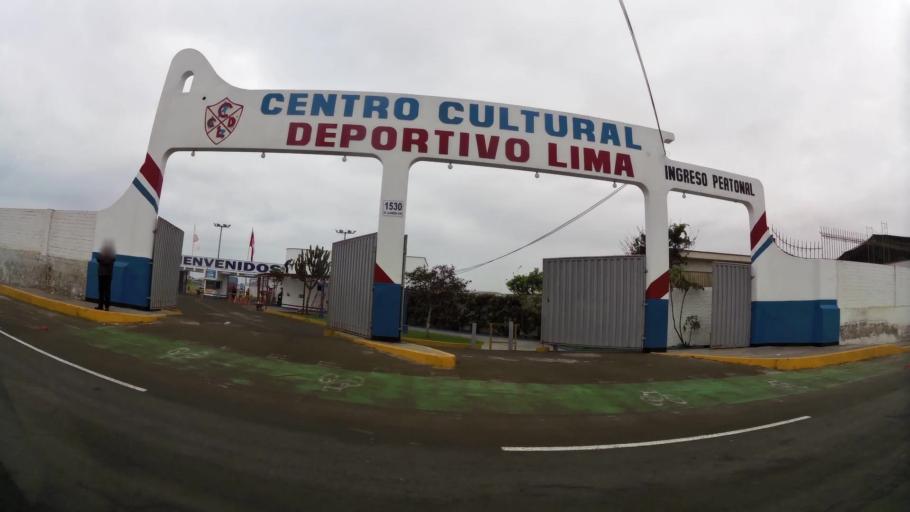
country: PE
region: Lima
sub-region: Lima
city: Surco
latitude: -12.2093
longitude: -77.0201
